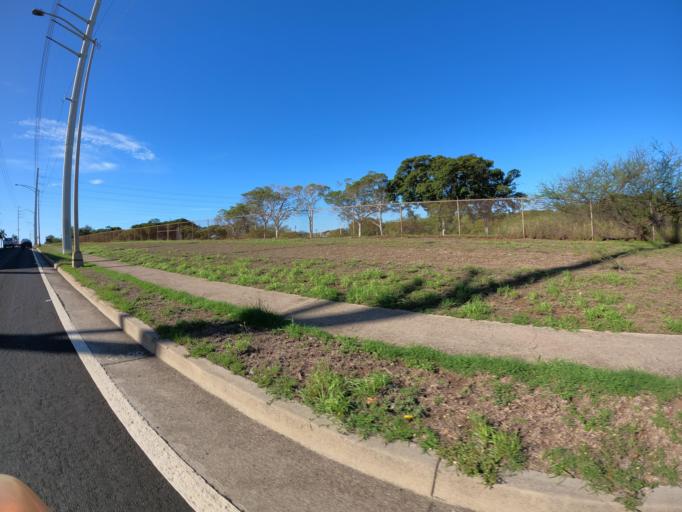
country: US
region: Hawaii
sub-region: Honolulu County
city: Halawa
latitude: 21.3536
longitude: -157.9317
